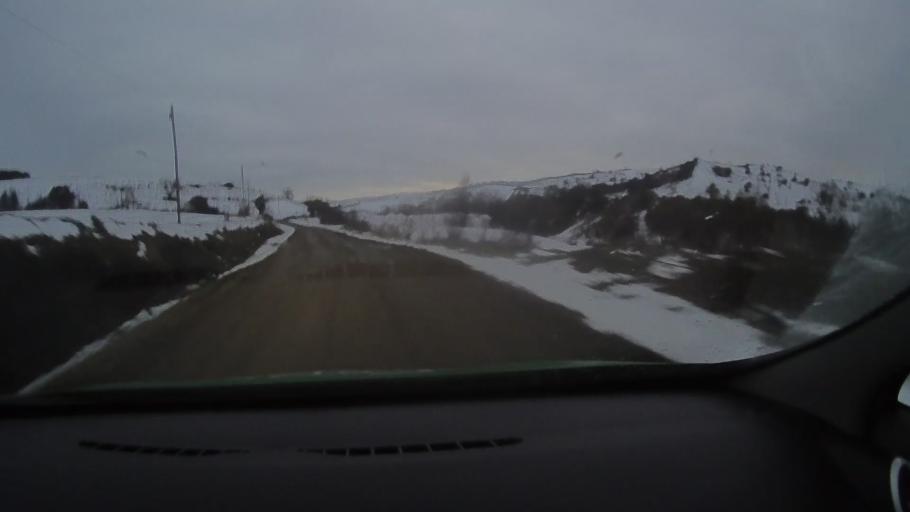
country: RO
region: Harghita
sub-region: Comuna Darjiu
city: Darjiu
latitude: 46.2059
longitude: 25.2438
